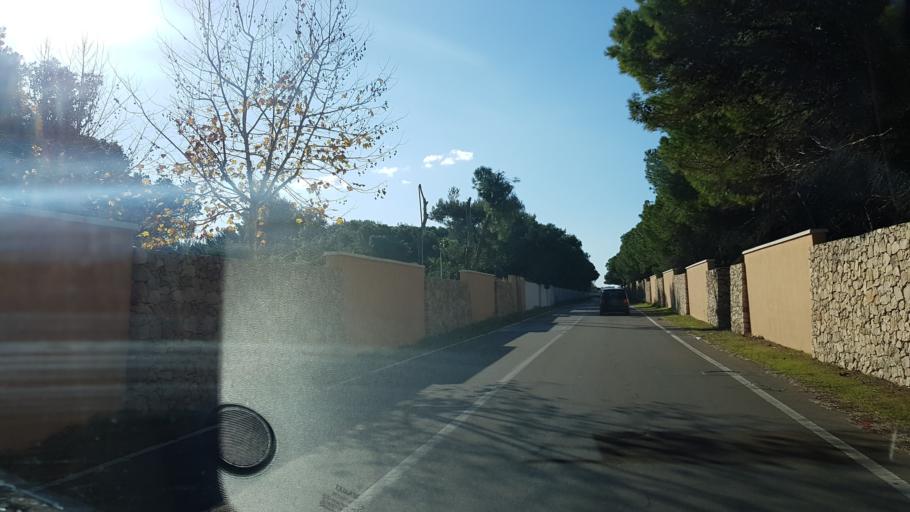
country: IT
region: Apulia
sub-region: Provincia di Lecce
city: Gallipoli
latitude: 40.0818
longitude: 18.0102
